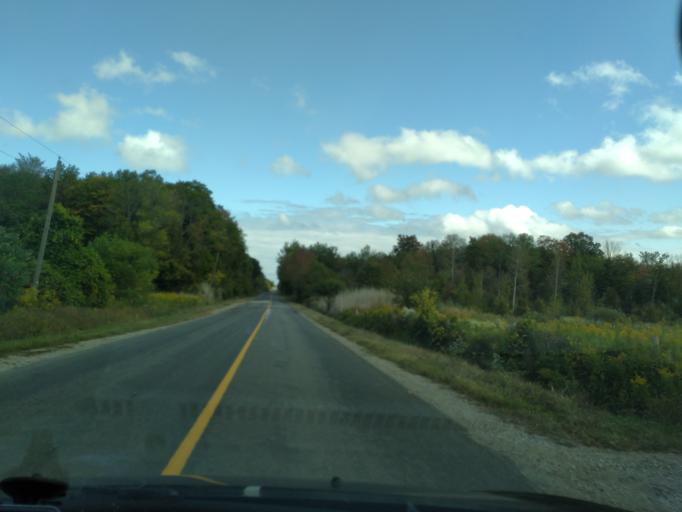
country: CA
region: Ontario
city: Innisfil
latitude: 44.2785
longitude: -79.5972
